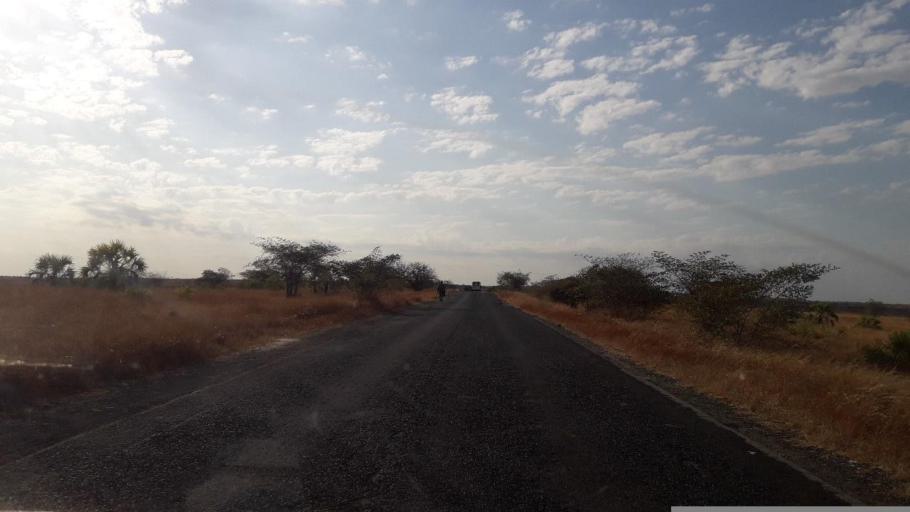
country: MG
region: Boeny
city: Mahajanga
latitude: -15.7735
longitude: 46.4916
